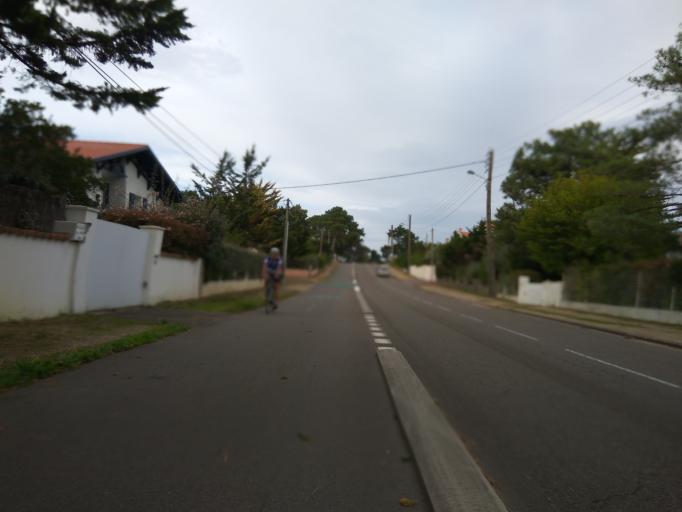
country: FR
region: Aquitaine
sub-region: Departement des Landes
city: Capbreton
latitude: 43.6428
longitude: -1.4414
